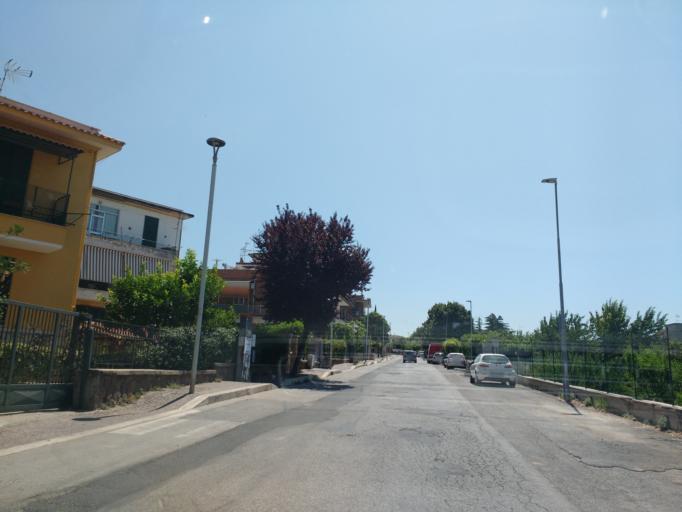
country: IT
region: Latium
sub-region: Citta metropolitana di Roma Capitale
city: Villa Adriana
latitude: 41.9494
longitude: 12.7719
